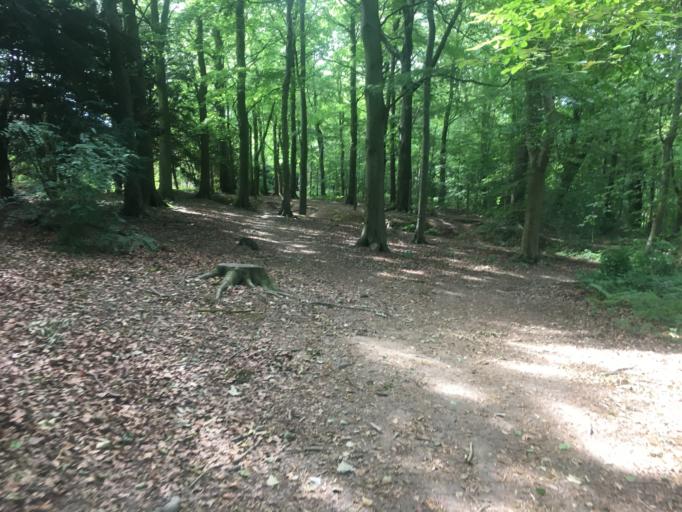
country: GB
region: England
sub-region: Sunderland
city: Washington
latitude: 54.8764
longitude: -1.5329
